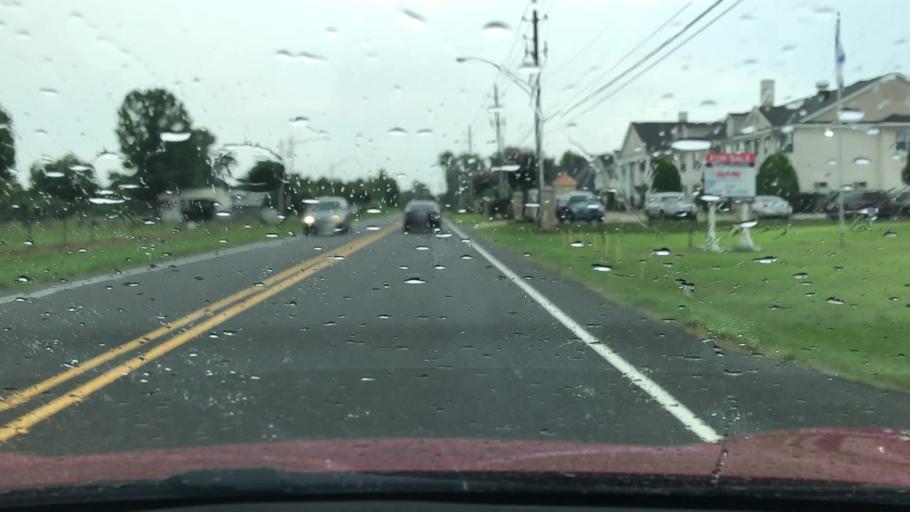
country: US
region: Louisiana
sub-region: Bossier Parish
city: Bossier City
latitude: 32.4214
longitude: -93.6941
